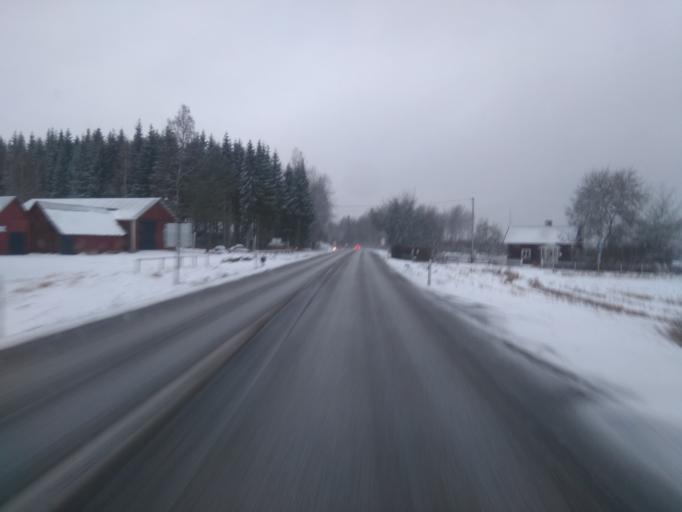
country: SE
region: Joenkoeping
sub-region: Eksjo Kommun
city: Eksjoe
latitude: 57.6354
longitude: 15.1008
